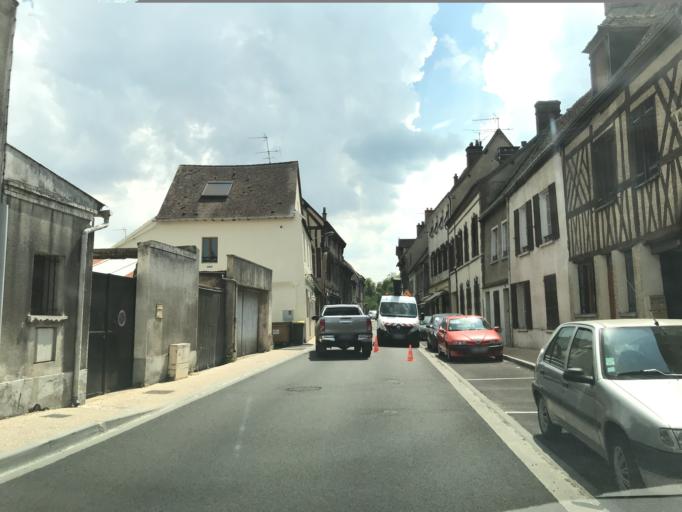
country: FR
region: Haute-Normandie
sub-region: Departement de l'Eure
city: Ivry-la-Bataille
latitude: 48.8839
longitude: 1.4589
